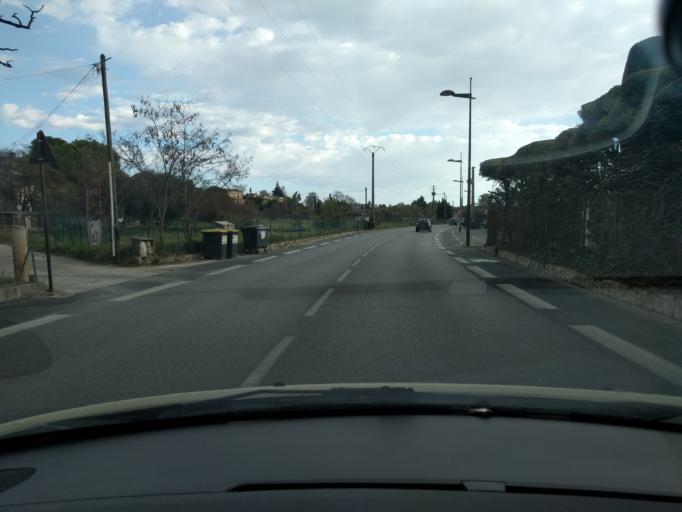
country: FR
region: Provence-Alpes-Cote d'Azur
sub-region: Departement des Alpes-Maritimes
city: Mouans-Sartoux
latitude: 43.6382
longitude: 6.9563
